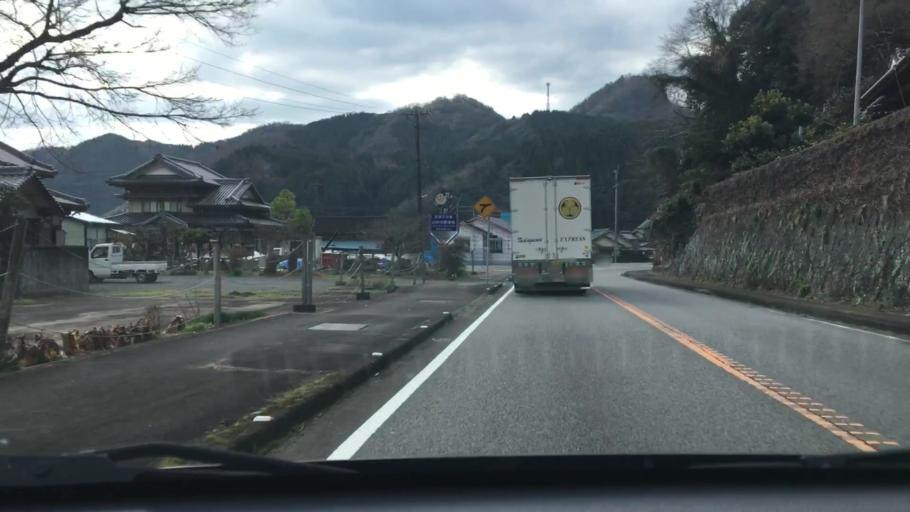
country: JP
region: Oita
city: Usuki
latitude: 33.0076
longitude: 131.7105
